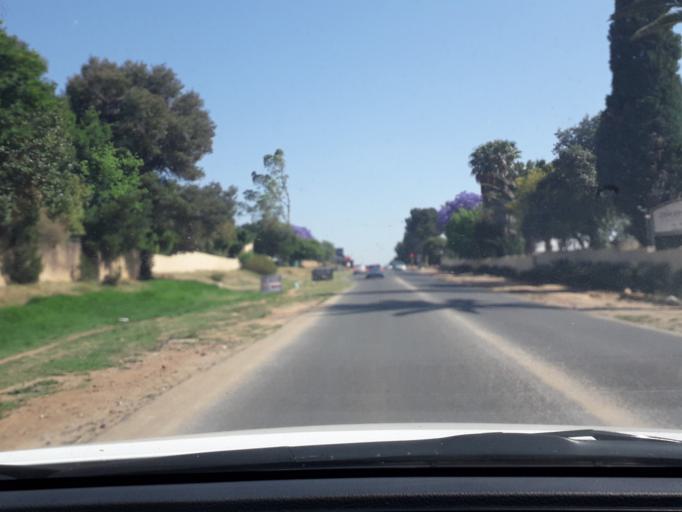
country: ZA
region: Gauteng
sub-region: City of Johannesburg Metropolitan Municipality
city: Roodepoort
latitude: -26.0892
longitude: 27.9586
